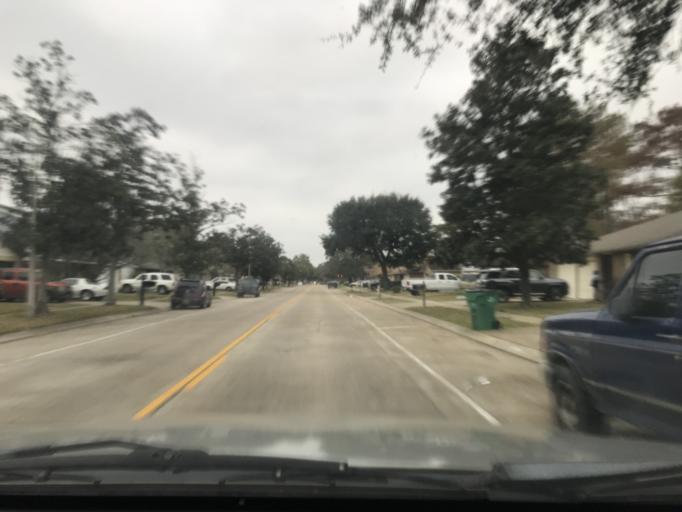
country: US
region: Louisiana
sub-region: Jefferson Parish
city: Woodmere
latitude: 29.8669
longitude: -90.0810
